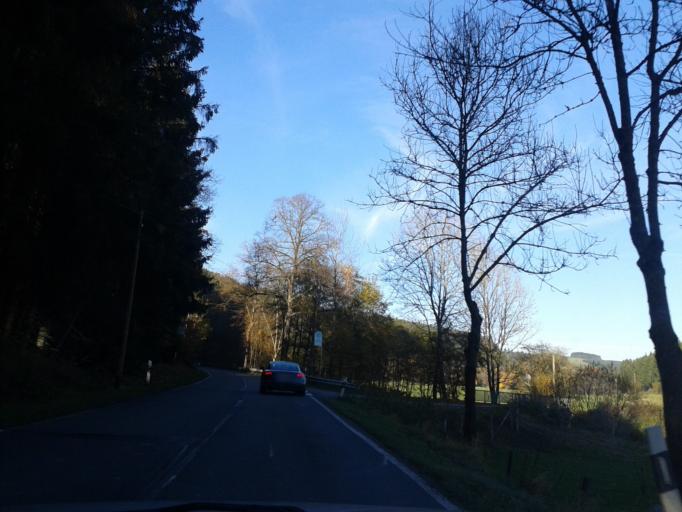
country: DE
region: North Rhine-Westphalia
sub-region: Regierungsbezirk Arnsberg
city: Bad Berleburg
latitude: 51.0858
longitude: 8.4257
